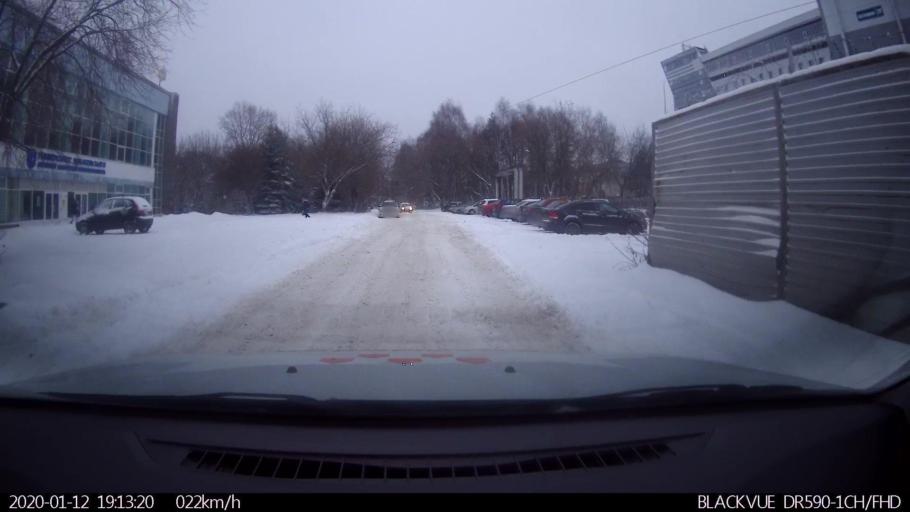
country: RU
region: Nizjnij Novgorod
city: Nizhniy Novgorod
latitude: 56.2951
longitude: 43.9778
